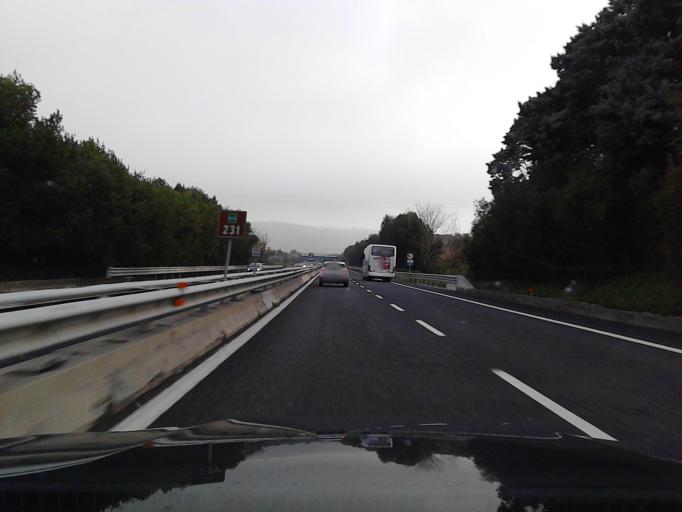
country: IT
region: Abruzzo
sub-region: Provincia di Chieti
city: Miglianico
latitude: 42.3820
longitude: 14.2905
